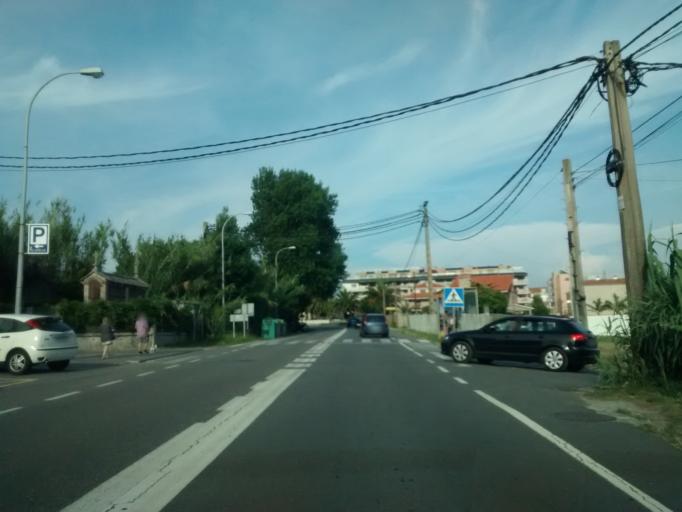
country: ES
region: Galicia
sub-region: Provincia de Pontevedra
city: Sanxenxo
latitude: 42.3921
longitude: -8.8317
